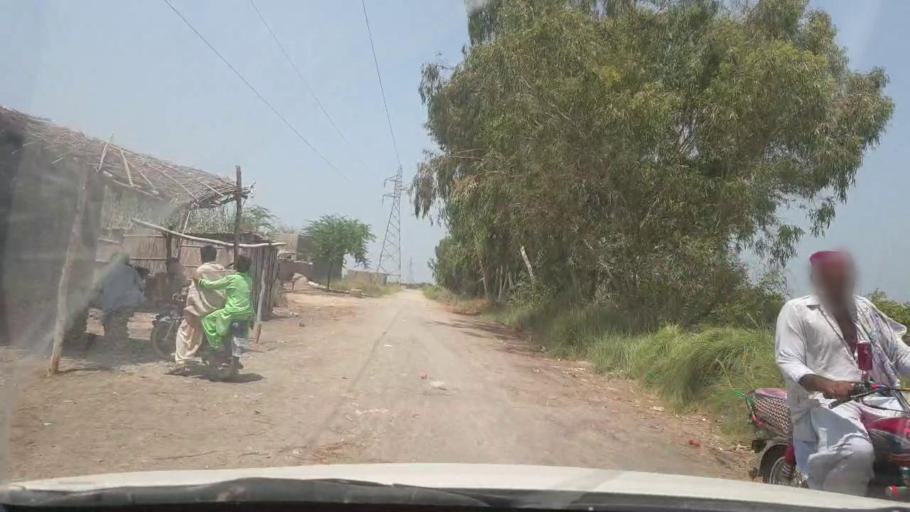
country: PK
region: Sindh
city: Lakhi
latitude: 27.8620
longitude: 68.6984
